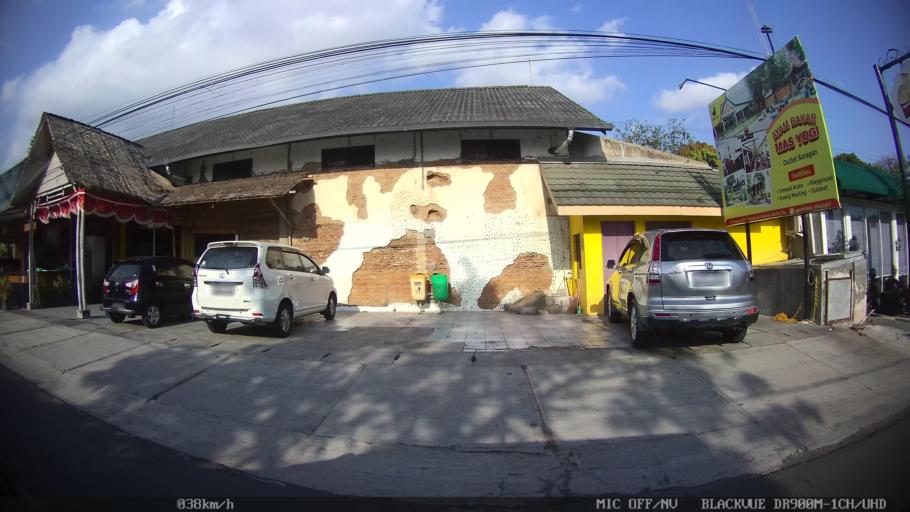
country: ID
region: Daerah Istimewa Yogyakarta
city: Yogyakarta
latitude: -7.7822
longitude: 110.3499
